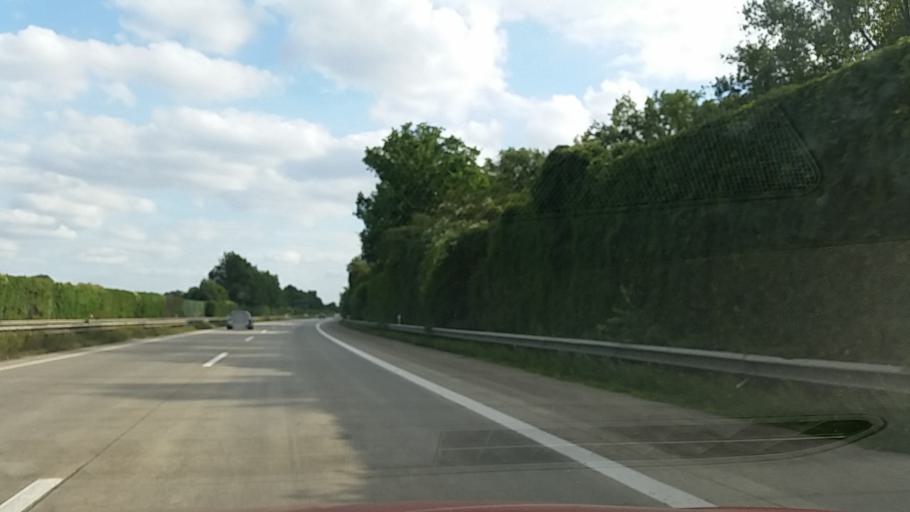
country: DE
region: Lower Saxony
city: Oyten
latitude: 53.0703
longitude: 8.9628
